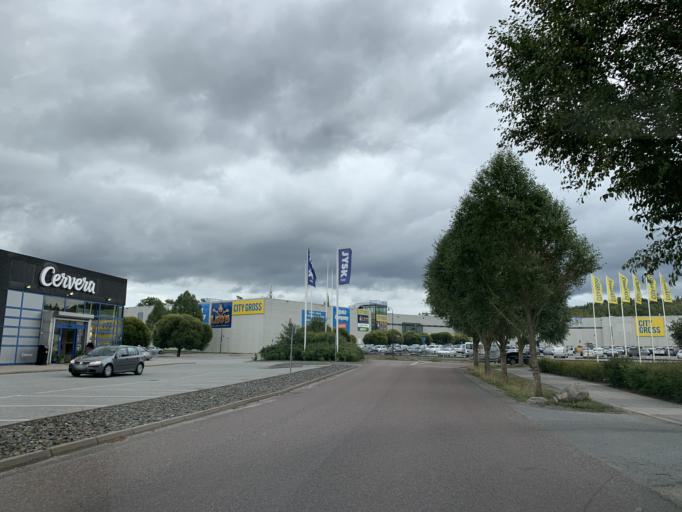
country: SE
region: Stockholm
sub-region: Huddinge Kommun
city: Segeltorp
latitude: 59.2677
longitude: 17.9220
